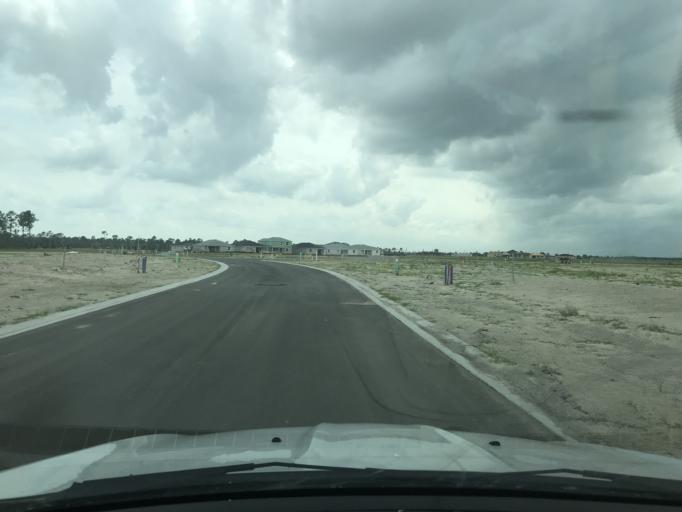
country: US
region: Florida
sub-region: Lee County
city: Olga
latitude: 26.7913
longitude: -81.7320
